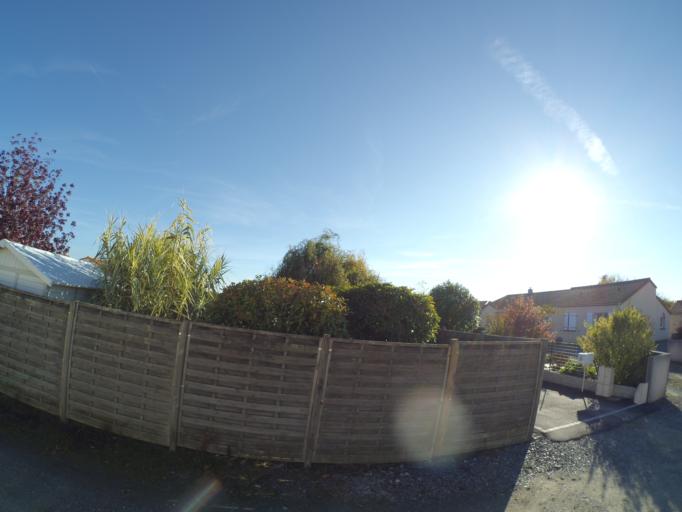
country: FR
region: Pays de la Loire
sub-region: Departement de la Loire-Atlantique
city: Saint-Lumine-de-Clisson
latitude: 47.0799
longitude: -1.3383
